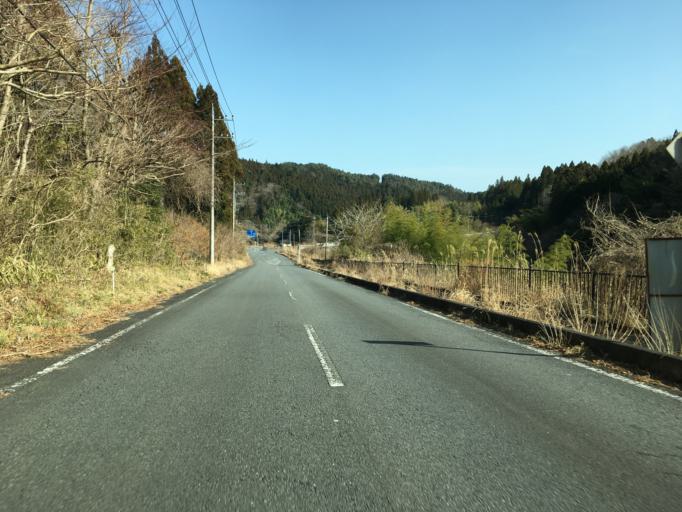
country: JP
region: Ibaraki
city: Kitaibaraki
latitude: 36.7969
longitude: 140.6461
